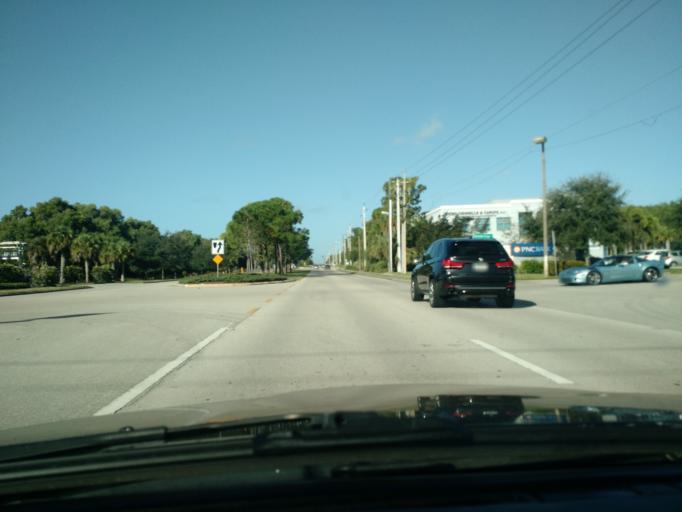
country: US
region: Florida
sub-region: Lee County
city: Bonita Springs
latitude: 26.3309
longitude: -81.7950
